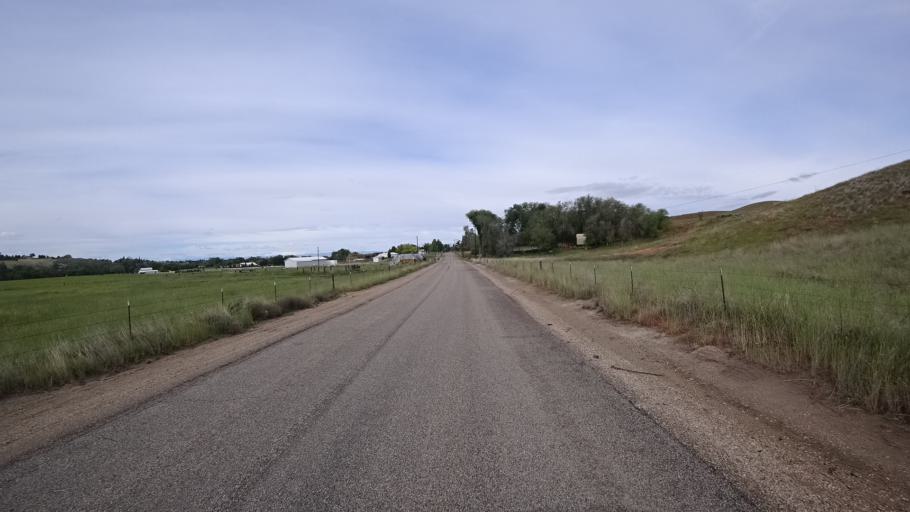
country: US
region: Idaho
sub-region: Ada County
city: Eagle
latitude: 43.7331
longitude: -116.3130
